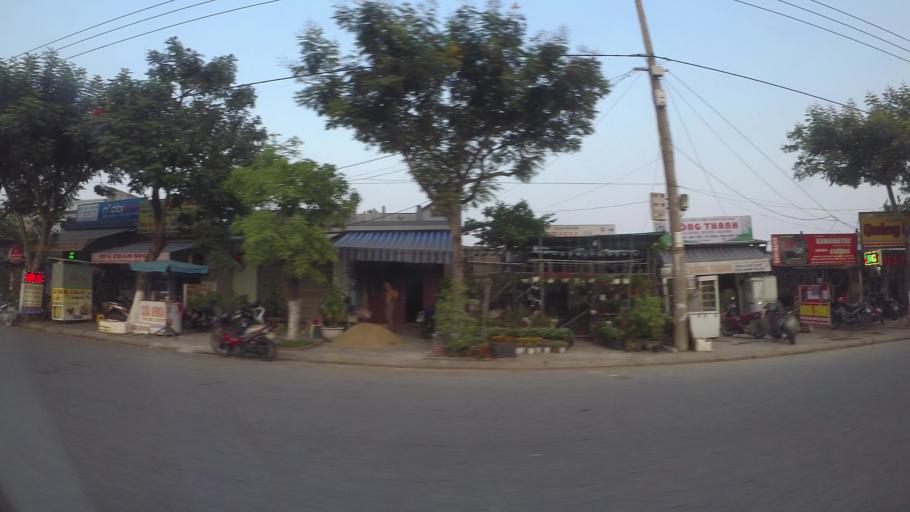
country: VN
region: Da Nang
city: Ngu Hanh Son
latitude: 15.9956
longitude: 108.2590
